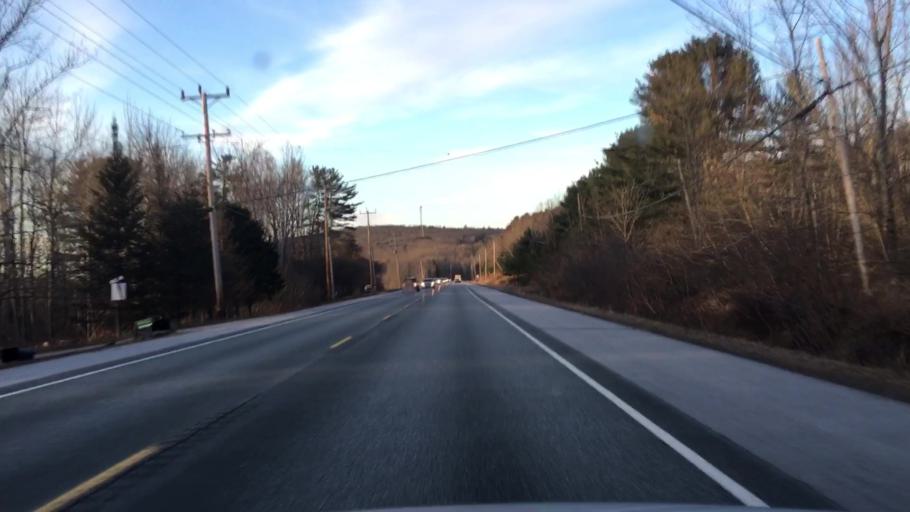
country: US
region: Maine
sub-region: Hancock County
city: Dedham
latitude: 44.7094
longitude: -68.6021
